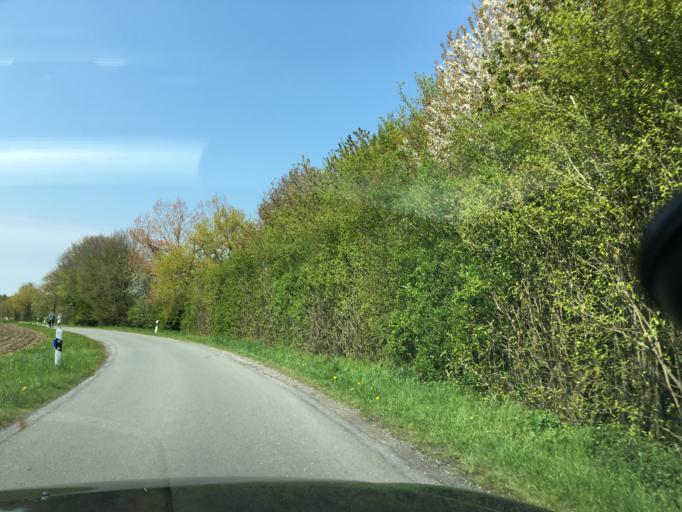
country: DE
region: North Rhine-Westphalia
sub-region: Regierungsbezirk Munster
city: Senden
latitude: 51.8224
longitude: 7.4682
